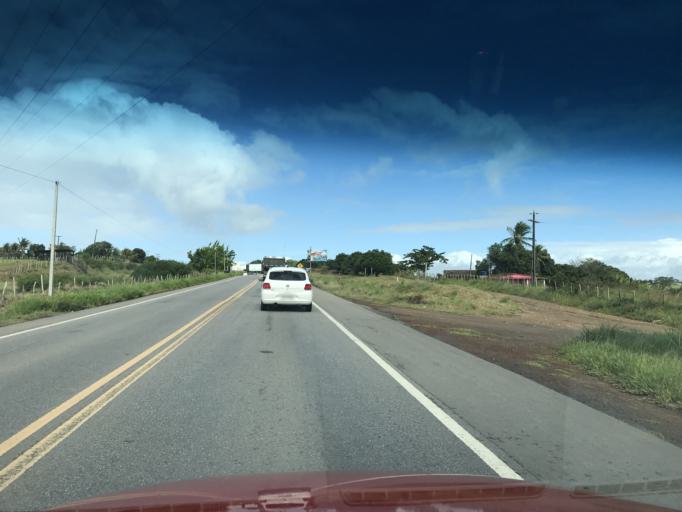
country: BR
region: Bahia
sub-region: Conceicao Do Almeida
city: Muritiba
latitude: -12.8939
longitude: -39.2324
